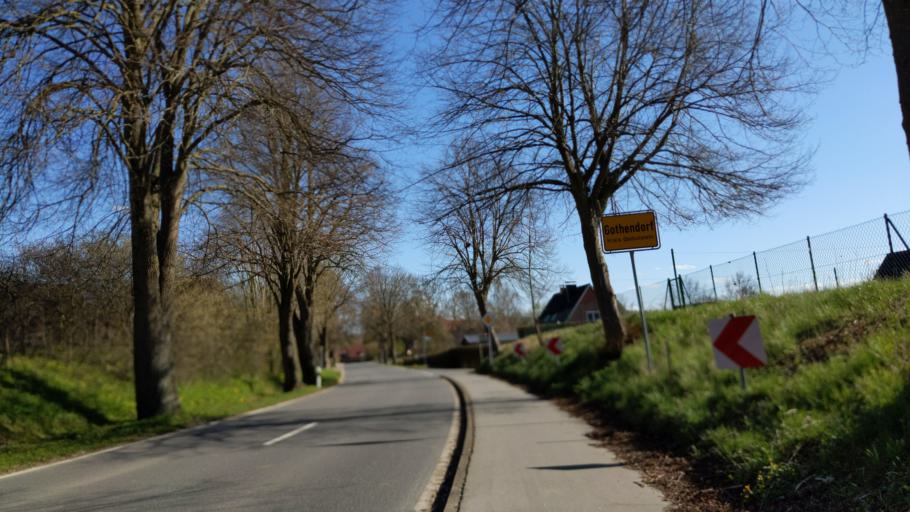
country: DE
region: Schleswig-Holstein
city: Eutin
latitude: 54.0953
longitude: 10.6133
